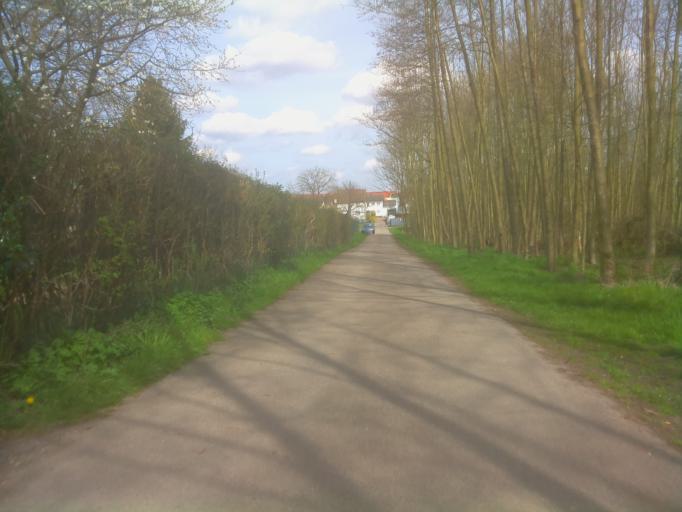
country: DE
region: Hesse
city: Lampertheim
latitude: 49.5843
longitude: 8.4837
